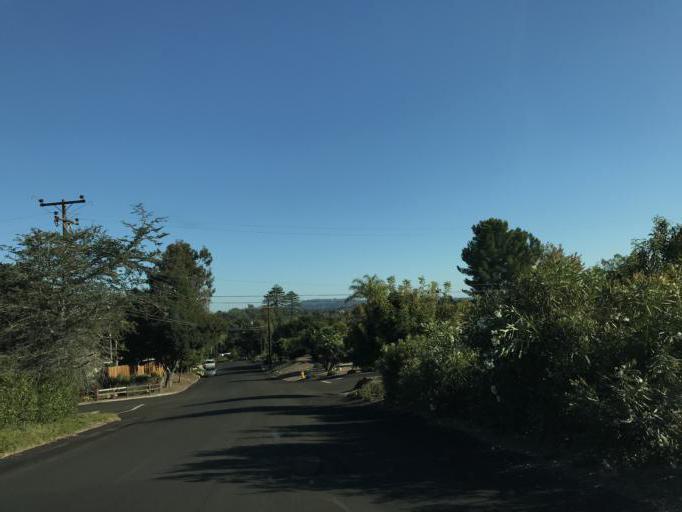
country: US
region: California
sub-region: Santa Barbara County
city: Goleta
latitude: 34.4609
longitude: -119.8186
